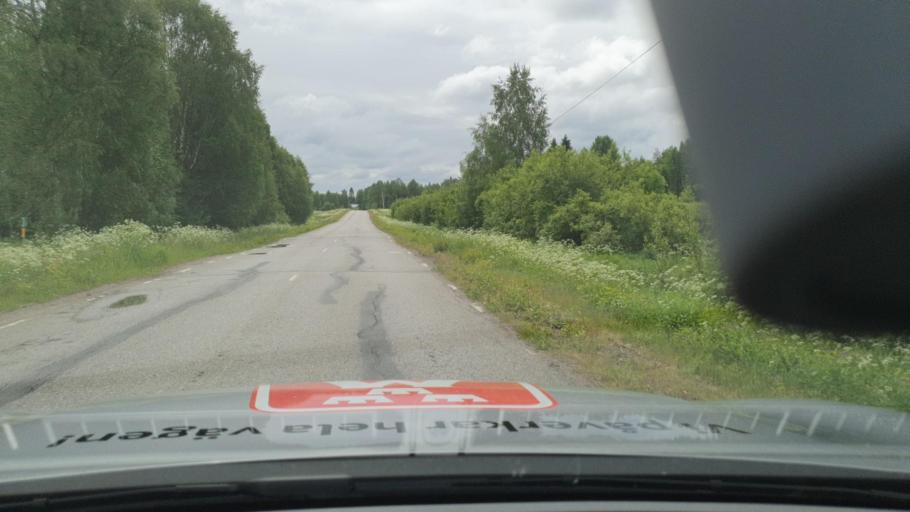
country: SE
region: Norrbotten
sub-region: Lulea Kommun
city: Ranea
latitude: 65.9247
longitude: 22.1463
